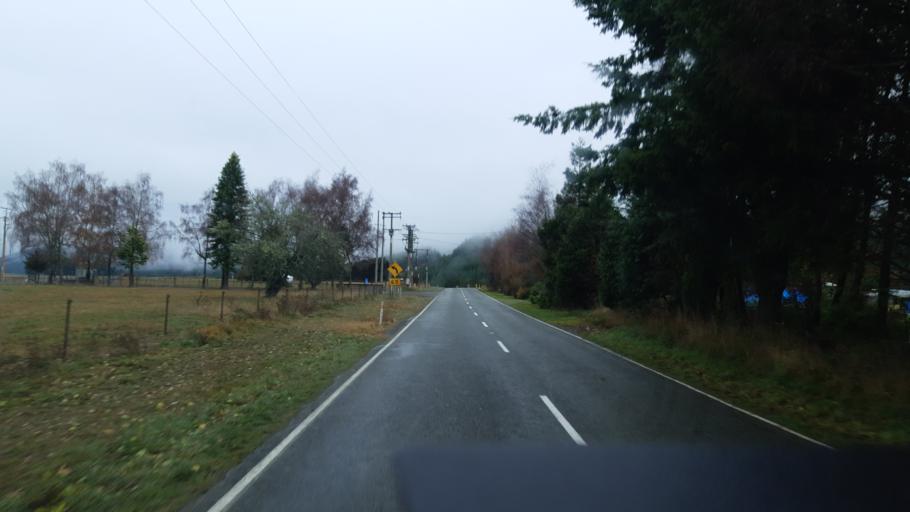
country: NZ
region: Tasman
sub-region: Tasman District
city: Wakefield
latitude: -41.6743
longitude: 172.8762
